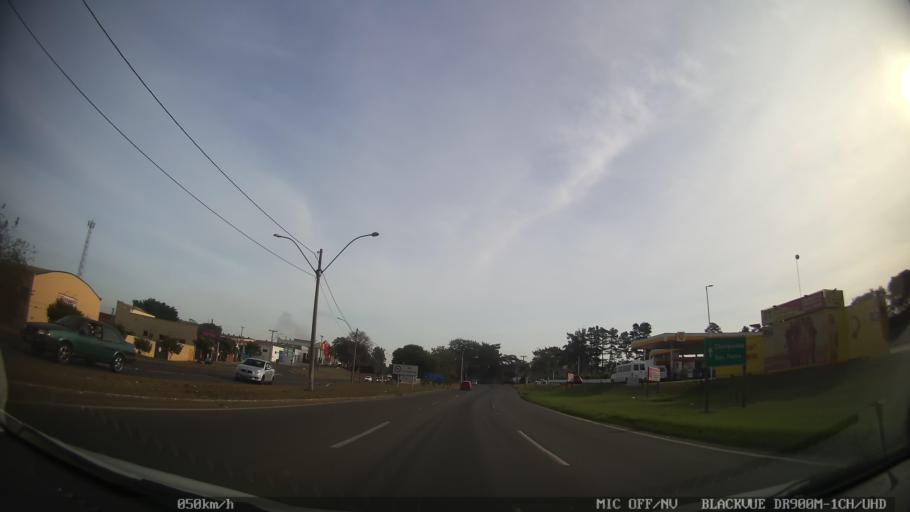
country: BR
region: Sao Paulo
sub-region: Piracicaba
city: Piracicaba
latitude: -22.6972
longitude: -47.6609
